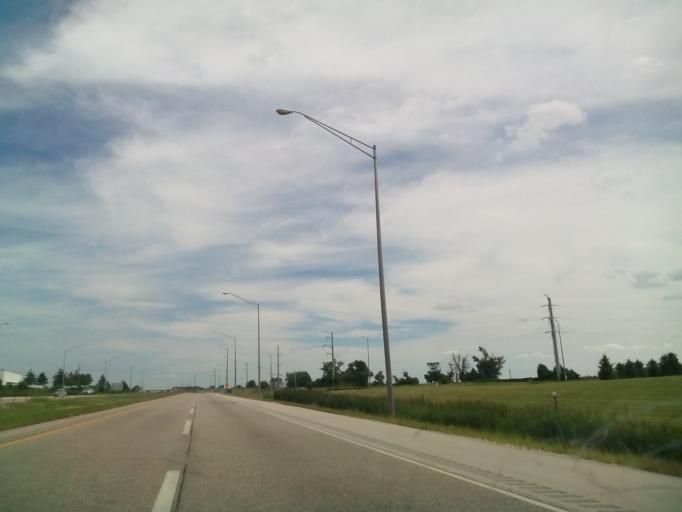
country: US
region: Illinois
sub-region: DeKalb County
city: DeKalb
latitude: 41.9012
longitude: -88.7379
